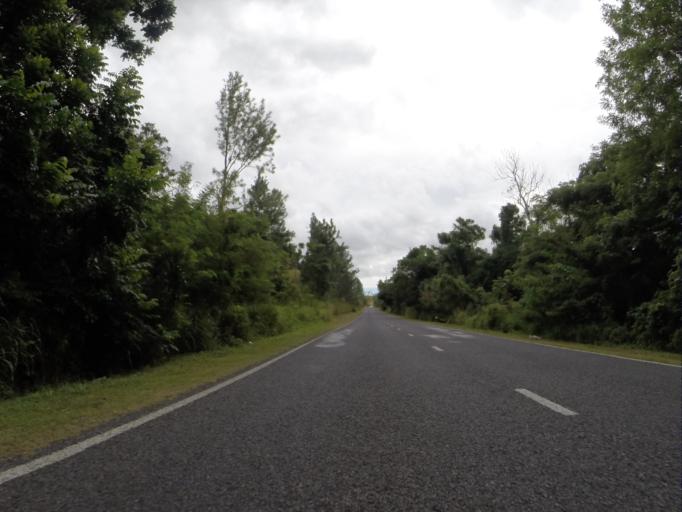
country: FJ
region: Western
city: Nadi
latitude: -18.0006
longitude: 177.3194
